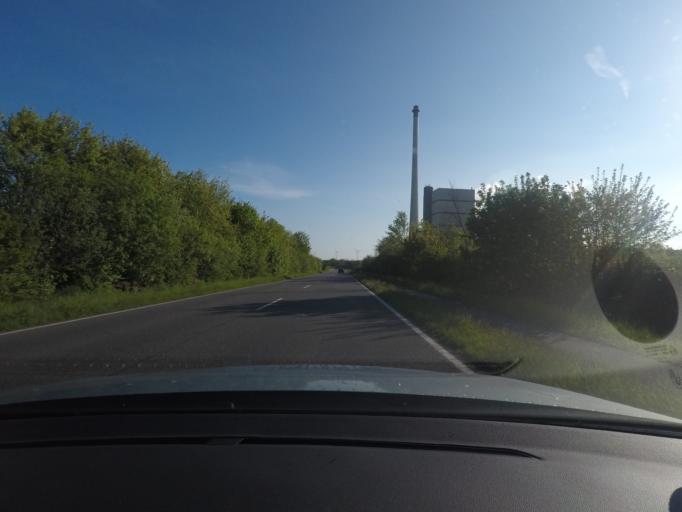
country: DE
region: Lower Saxony
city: Schoningen
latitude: 52.1675
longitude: 10.9709
